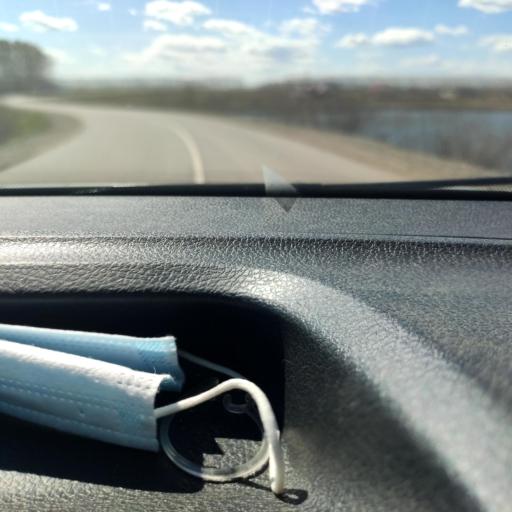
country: RU
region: Bashkortostan
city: Alekseyevka
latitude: 54.7284
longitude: 55.1753
